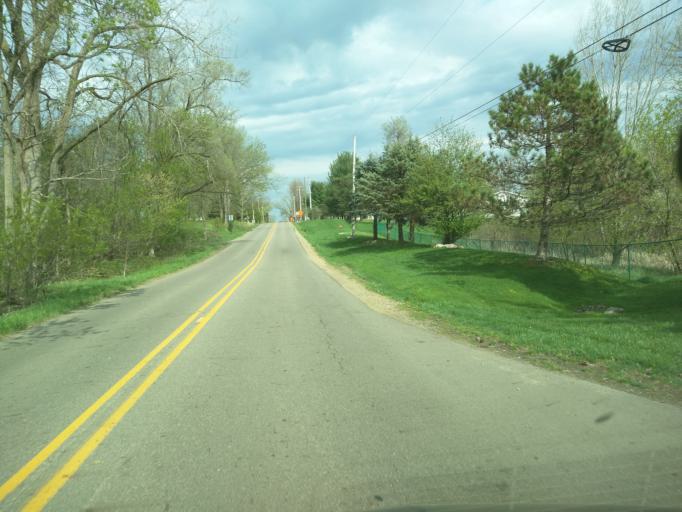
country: US
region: Michigan
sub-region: Eaton County
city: Dimondale
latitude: 42.6831
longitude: -84.6115
